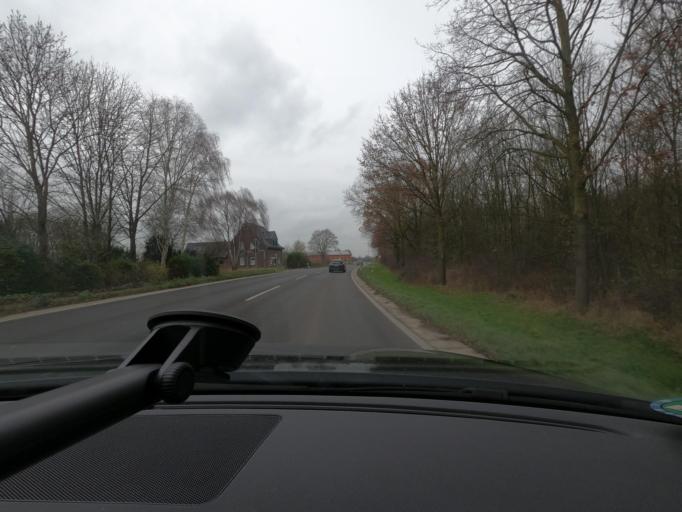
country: DE
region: North Rhine-Westphalia
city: Kempen
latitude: 51.3807
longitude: 6.3881
